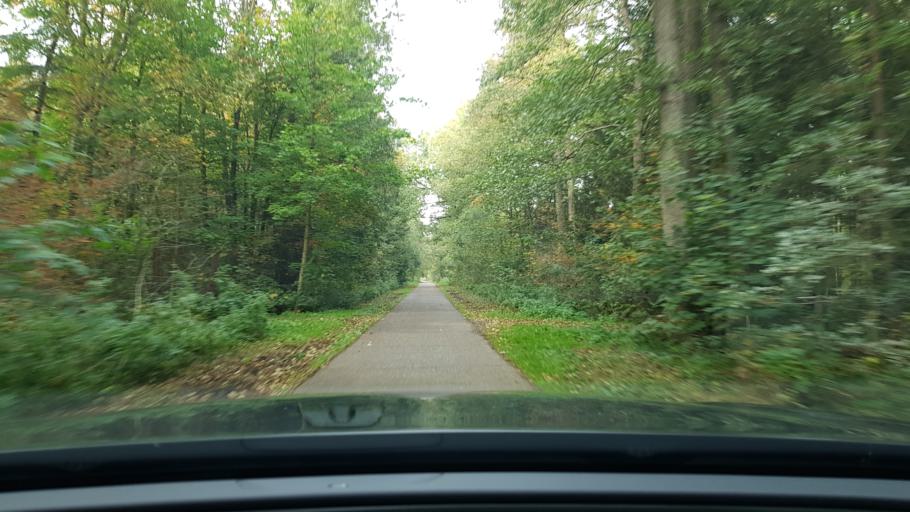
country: DE
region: Lower Saxony
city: Beverstedt
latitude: 53.4192
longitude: 8.8116
